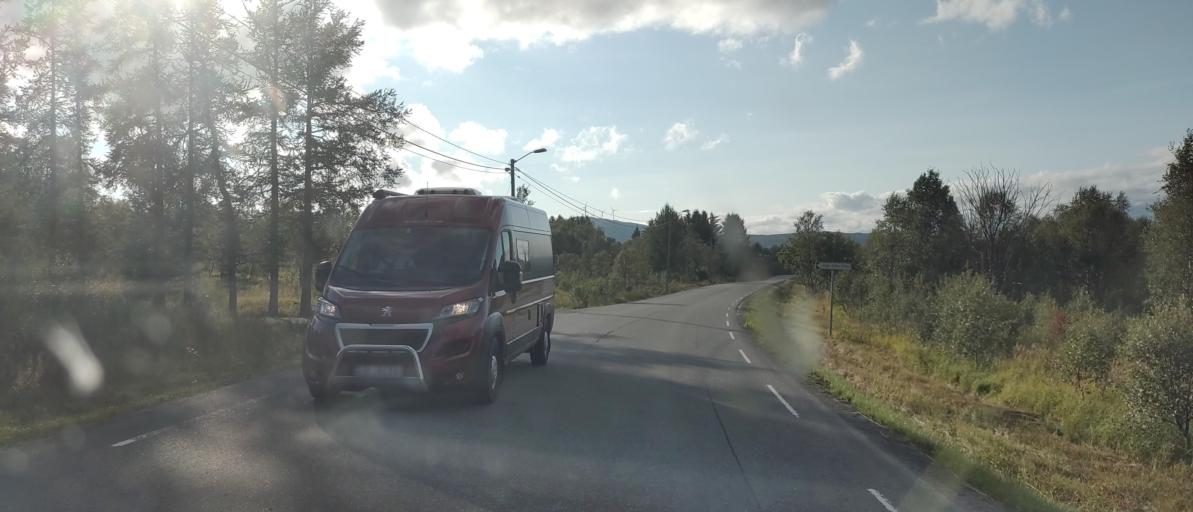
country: NO
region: Nordland
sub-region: Sortland
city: Sortland
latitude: 68.7209
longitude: 15.5084
